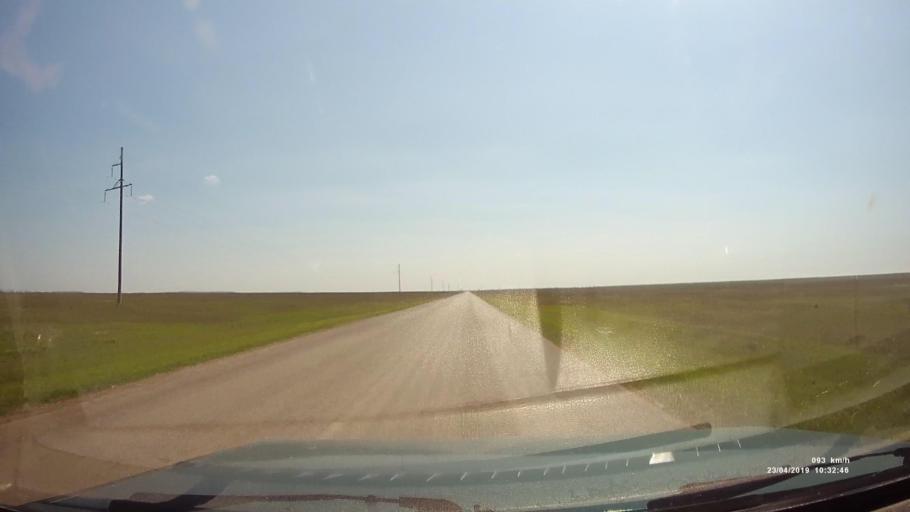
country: RU
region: Kalmykiya
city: Yashalta
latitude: 46.5780
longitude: 42.5843
